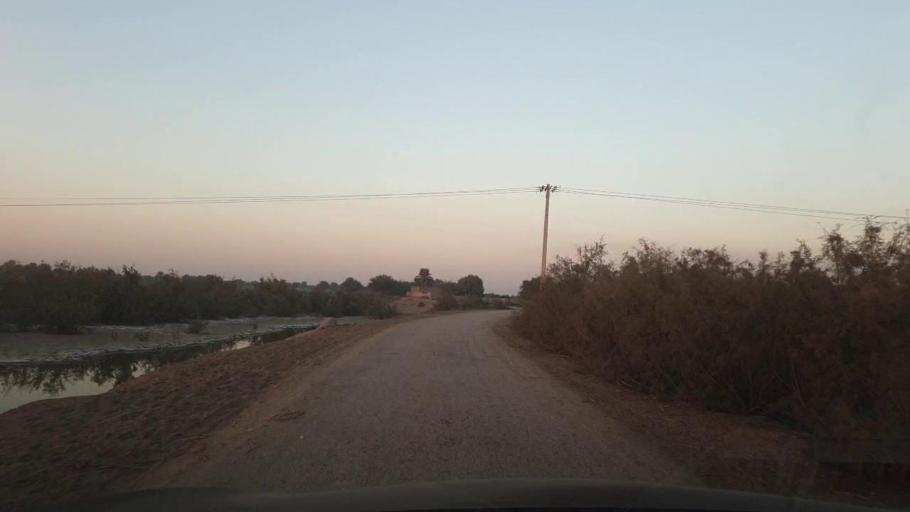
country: PK
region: Sindh
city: Ubauro
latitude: 28.1670
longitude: 69.6357
